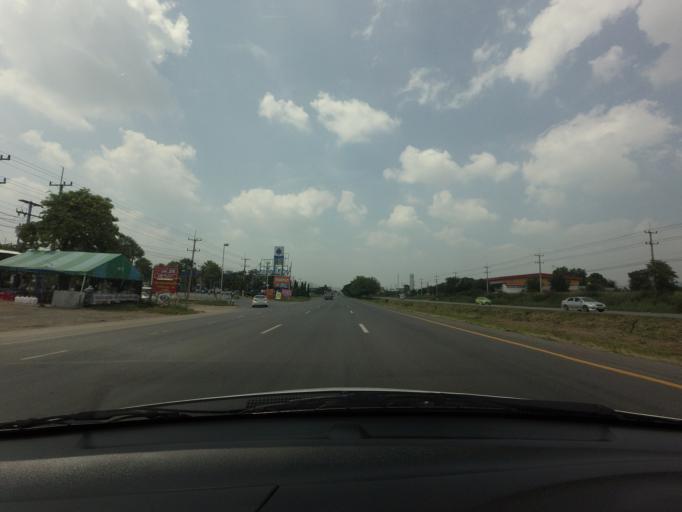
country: TH
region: Nakhon Ratchasima
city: Pak Chong
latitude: 14.6669
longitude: 101.4343
